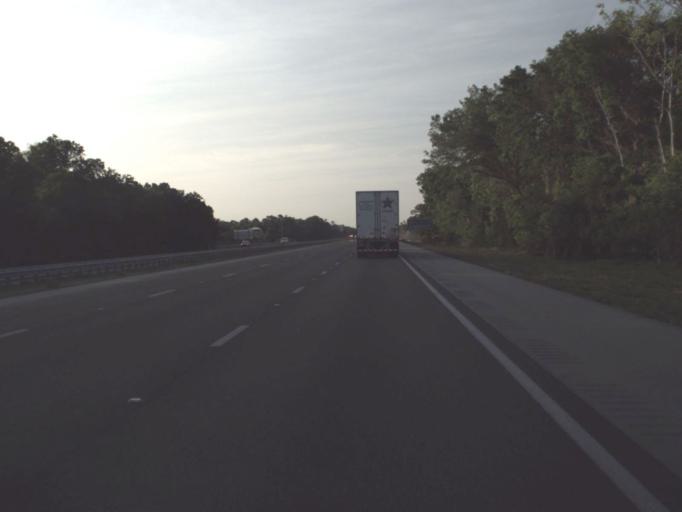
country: US
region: Florida
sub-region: Brevard County
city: Mims
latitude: 28.6775
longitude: -80.8742
